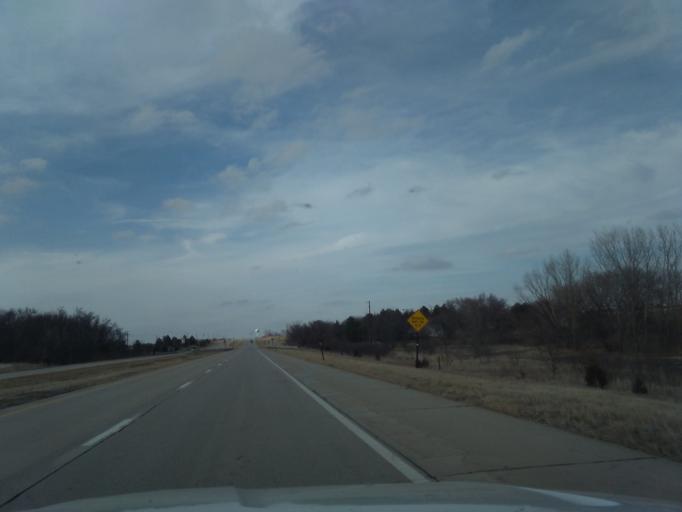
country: US
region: Nebraska
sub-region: Lancaster County
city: Hickman
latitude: 40.4836
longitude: -96.7044
